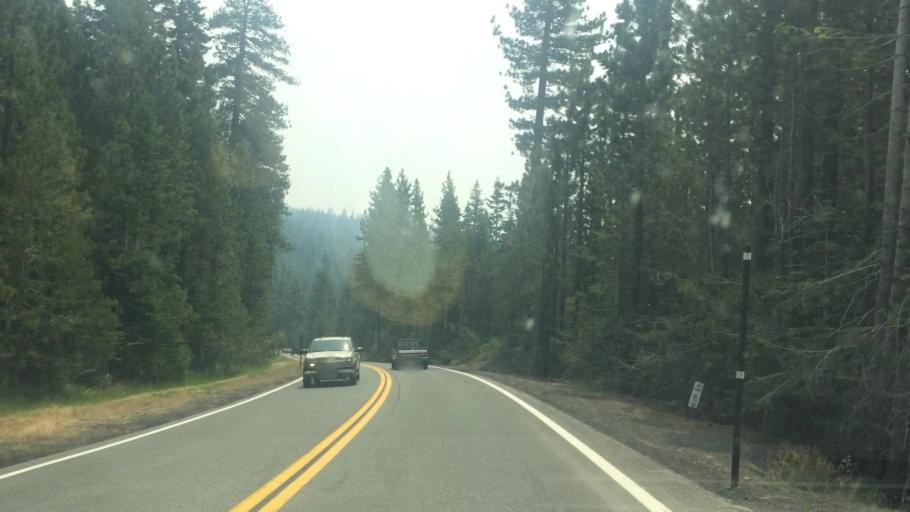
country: US
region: California
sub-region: El Dorado County
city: South Lake Tahoe
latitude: 38.6827
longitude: -120.1201
